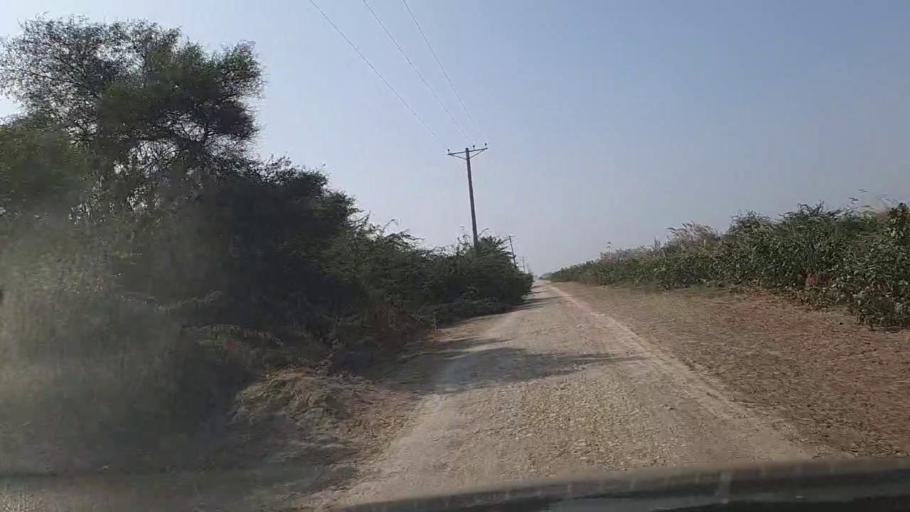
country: PK
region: Sindh
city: Gharo
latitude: 24.6878
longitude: 67.6062
